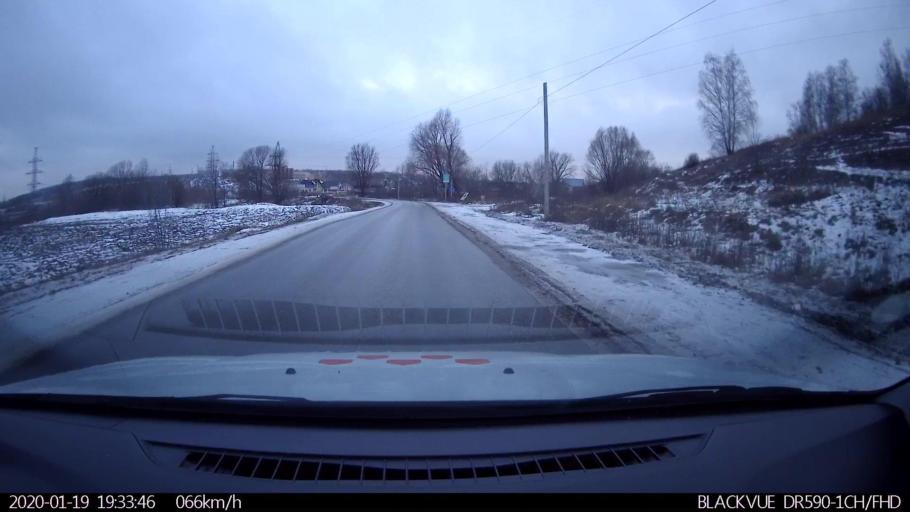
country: RU
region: Nizjnij Novgorod
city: Afonino
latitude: 56.2419
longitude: 44.0901
